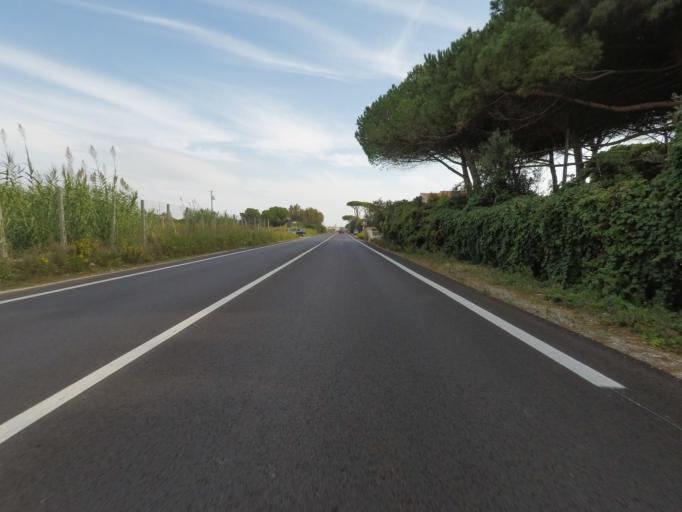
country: IT
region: Latium
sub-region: Citta metropolitana di Roma Capitale
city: Santa Marinella
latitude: 42.0471
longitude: 11.8227
